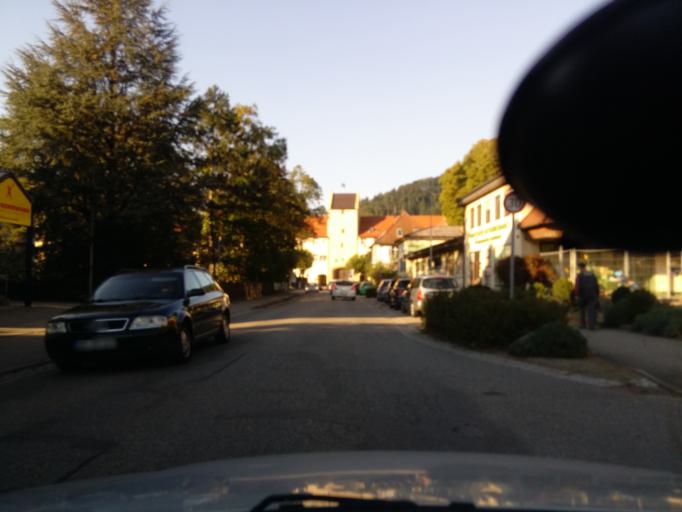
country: DE
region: Baden-Wuerttemberg
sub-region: Freiburg Region
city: Wolfach
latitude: 48.2965
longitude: 8.2214
